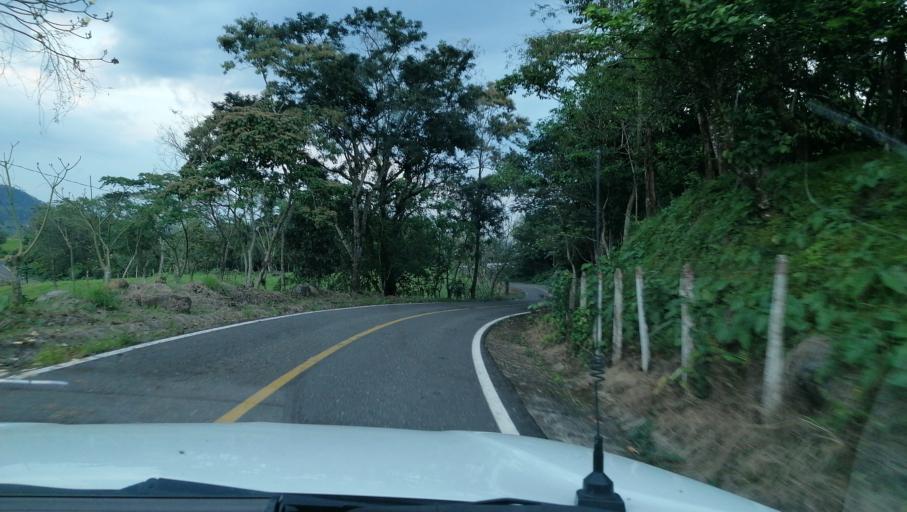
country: MX
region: Chiapas
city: Pichucalco
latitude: 17.5277
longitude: -93.1548
